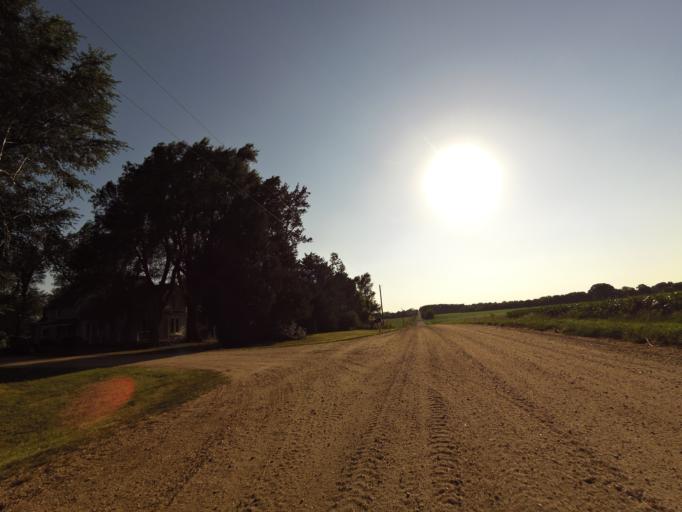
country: US
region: Kansas
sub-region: McPherson County
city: Inman
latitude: 38.1883
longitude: -97.8538
